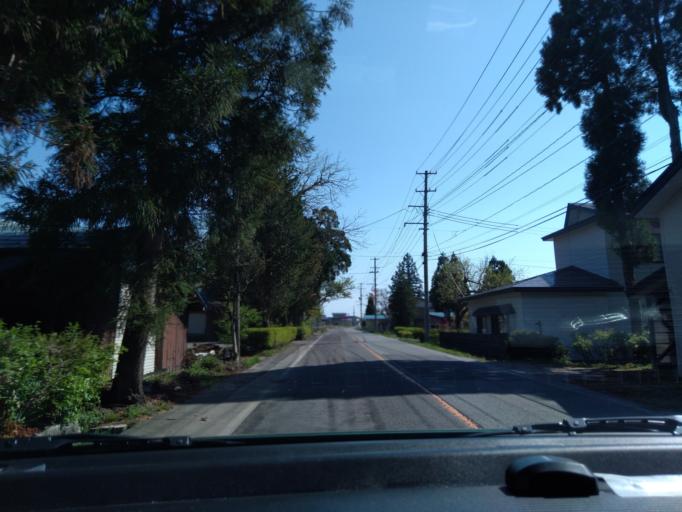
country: JP
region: Akita
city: Kakunodatemachi
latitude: 39.4881
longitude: 140.5925
